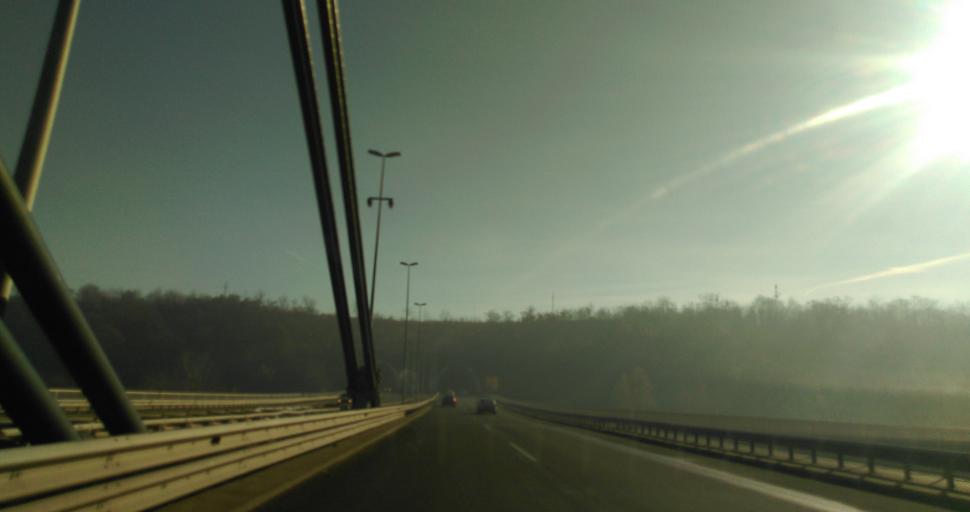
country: RS
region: Autonomna Pokrajina Vojvodina
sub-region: Juznobacki Okrug
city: Novi Sad
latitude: 45.2318
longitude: 19.8524
